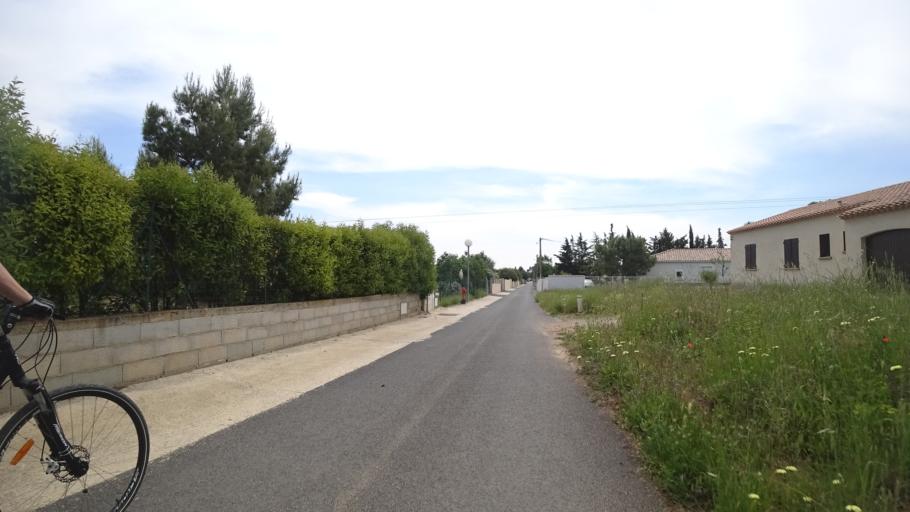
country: FR
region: Languedoc-Roussillon
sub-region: Departement de l'Aude
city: Canet
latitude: 43.2530
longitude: 2.8228
